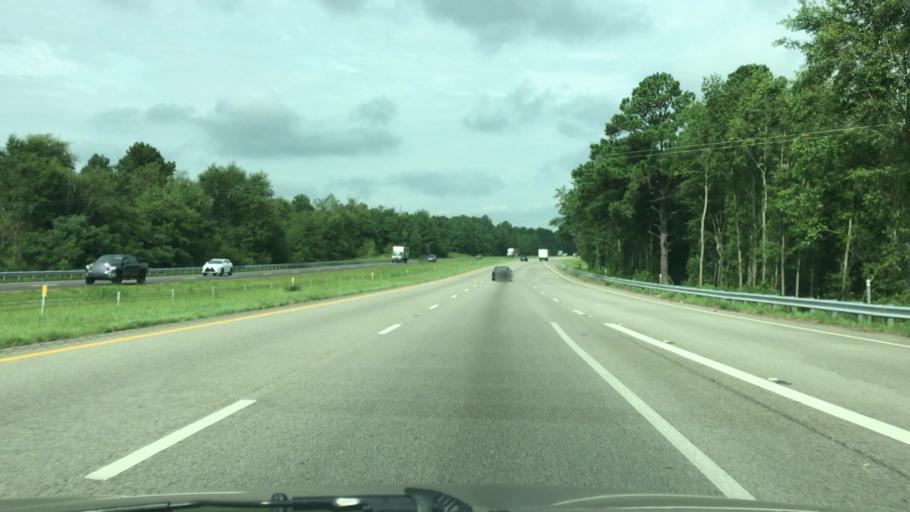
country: US
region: South Carolina
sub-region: Aiken County
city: Aiken
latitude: 33.6376
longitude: -81.7460
